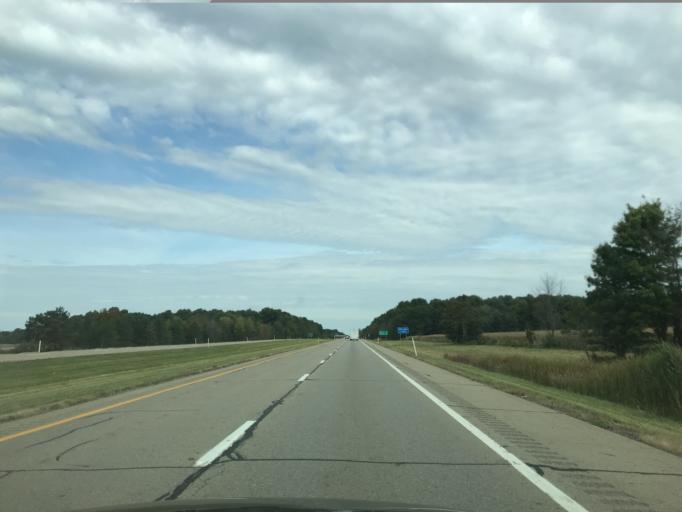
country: US
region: Ohio
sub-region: Ashtabula County
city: Roaming Shores
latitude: 41.5468
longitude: -80.7132
